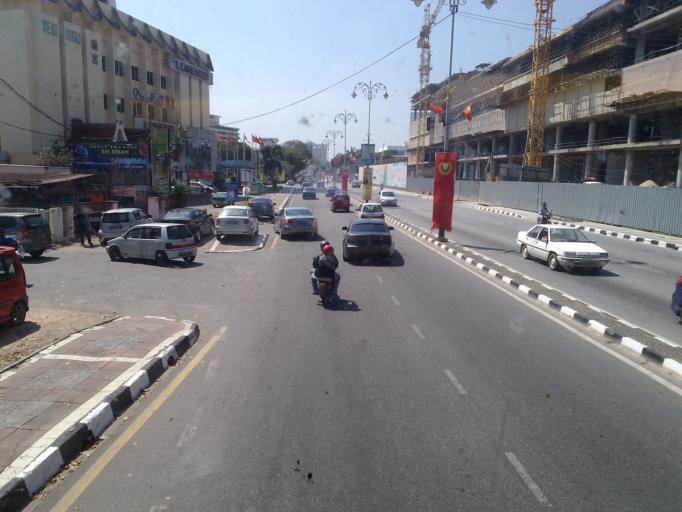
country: MY
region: Kedah
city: Alor Setar
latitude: 6.1259
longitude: 100.3671
